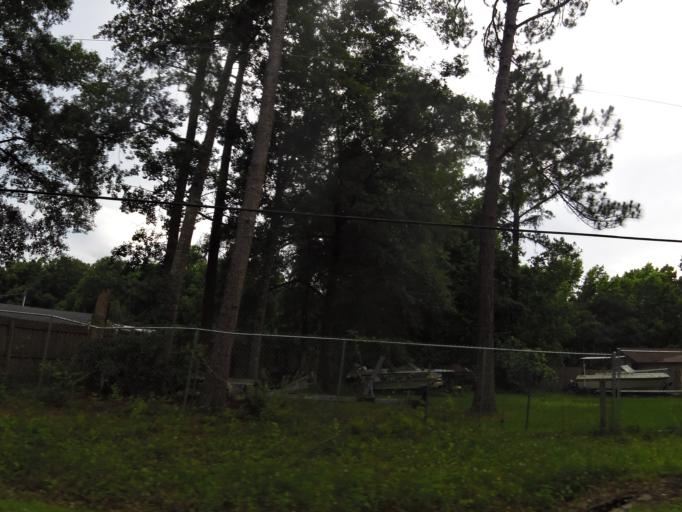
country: US
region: Florida
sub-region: Nassau County
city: Nassau Village-Ratliff
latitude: 30.5479
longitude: -81.7295
